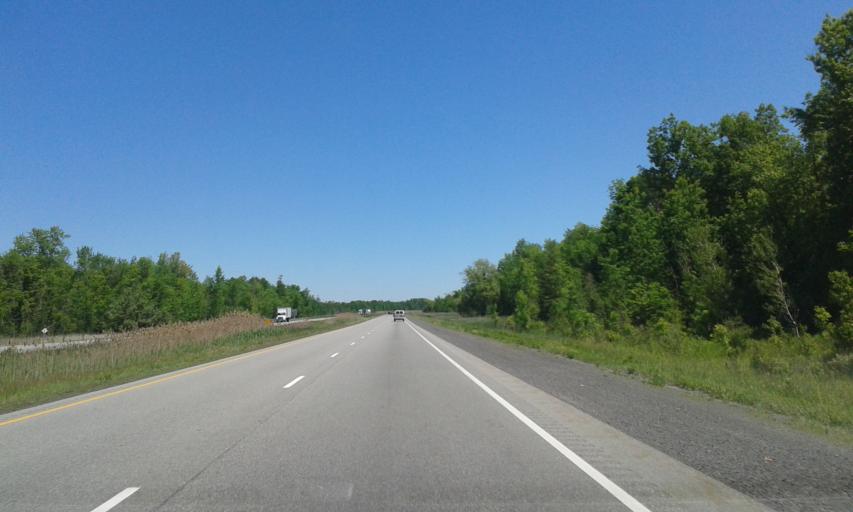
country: CA
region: Ontario
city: Prescott
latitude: 44.7658
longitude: -75.4645
